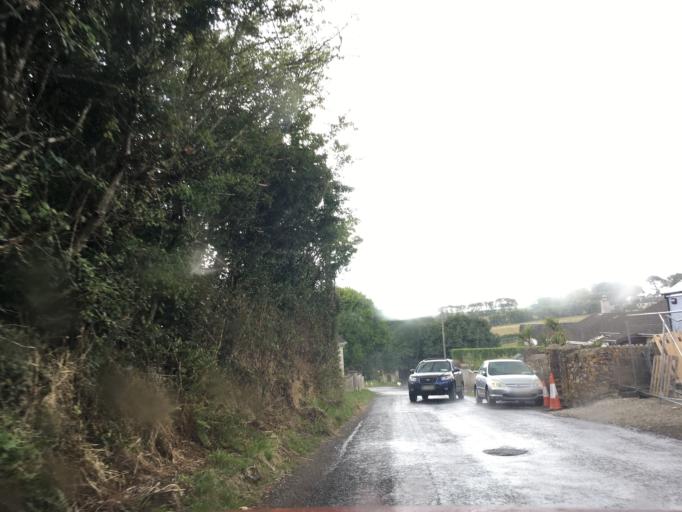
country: IE
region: Munster
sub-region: County Cork
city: Crosshaven
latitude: 51.7858
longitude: -8.3059
